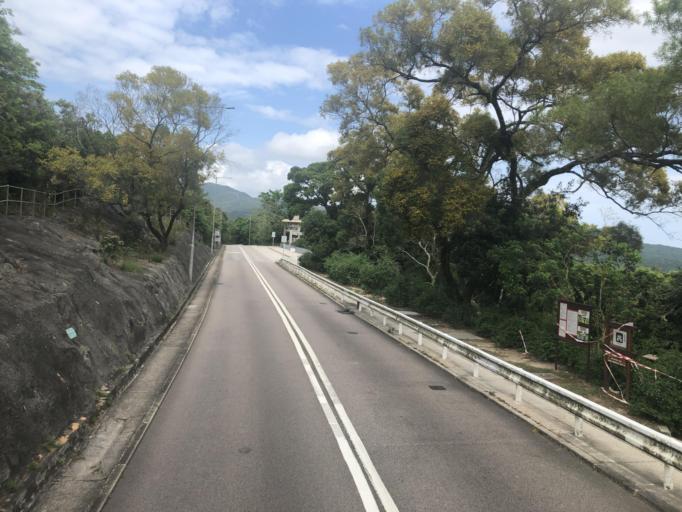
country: HK
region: Sai Kung
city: Sai Kung
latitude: 22.3865
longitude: 114.3051
